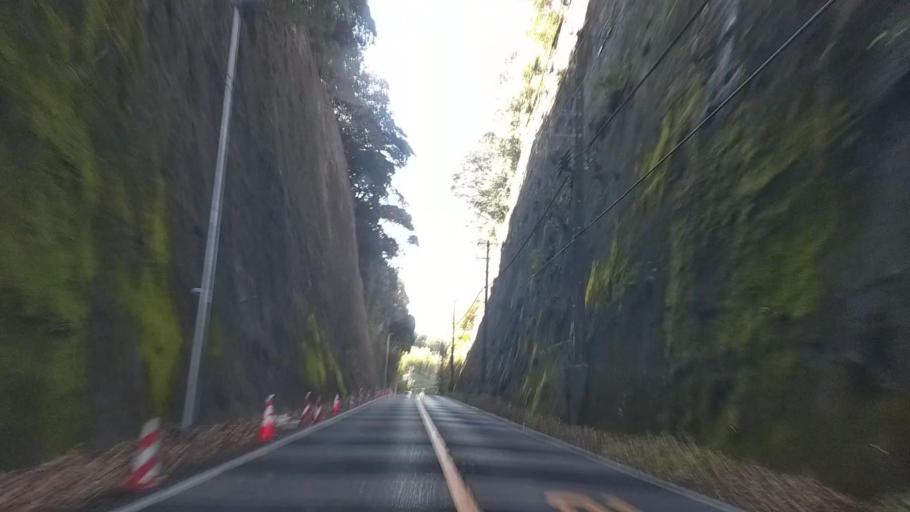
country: JP
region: Chiba
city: Tateyama
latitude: 34.9612
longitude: 139.8549
